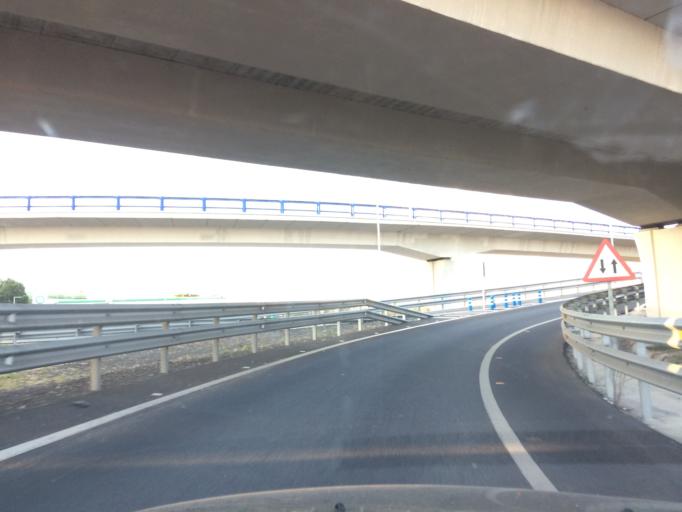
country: ES
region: Andalusia
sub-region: Provincia de Malaga
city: Torremolinos
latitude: 36.6740
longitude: -4.4858
